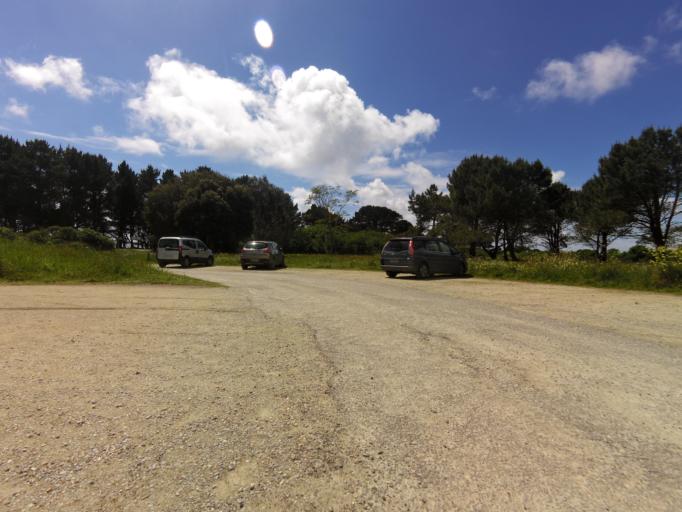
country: FR
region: Brittany
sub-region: Departement du Morbihan
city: Locmariaquer
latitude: 47.5556
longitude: -2.9302
